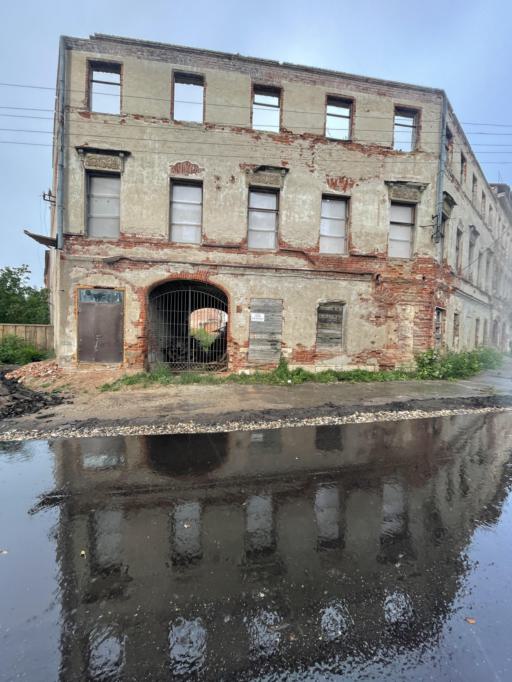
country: RU
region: Tverskaya
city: Vyshniy Volochek
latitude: 57.5850
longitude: 34.5544
